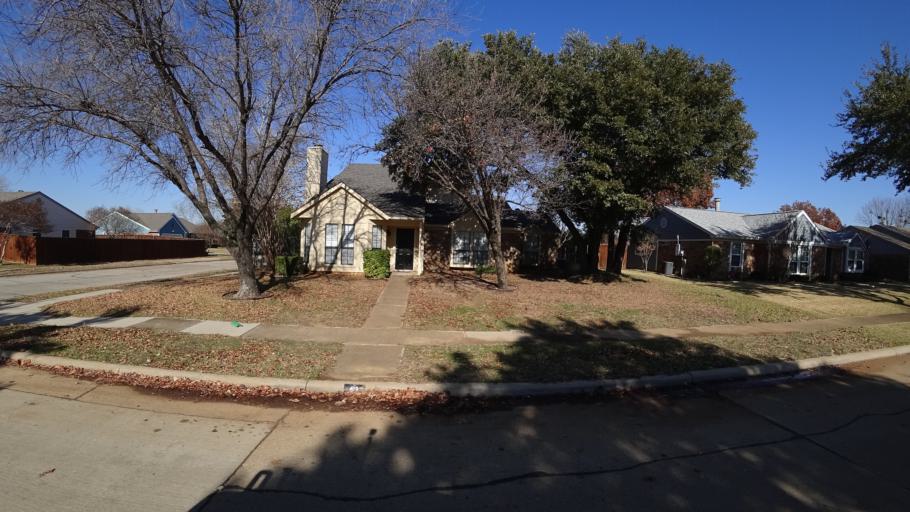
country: US
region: Texas
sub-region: Denton County
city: Lewisville
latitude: 33.0083
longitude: -97.0007
